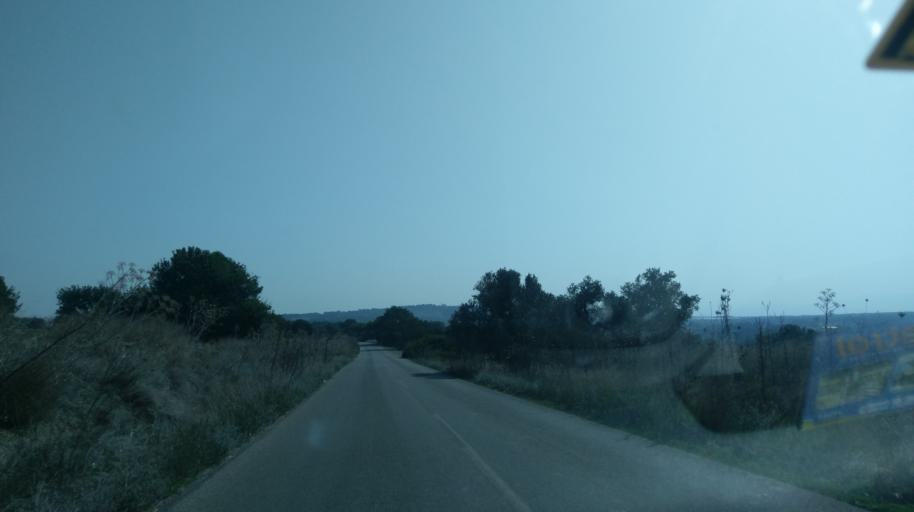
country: CY
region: Lefkosia
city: Morfou
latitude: 35.3329
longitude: 33.0325
